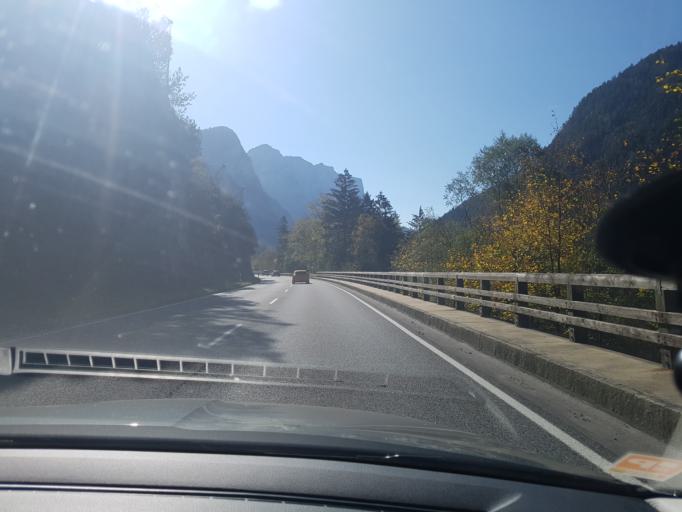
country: DE
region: Bavaria
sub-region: Upper Bavaria
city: Bad Reichenhall
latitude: 47.7001
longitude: 12.8515
